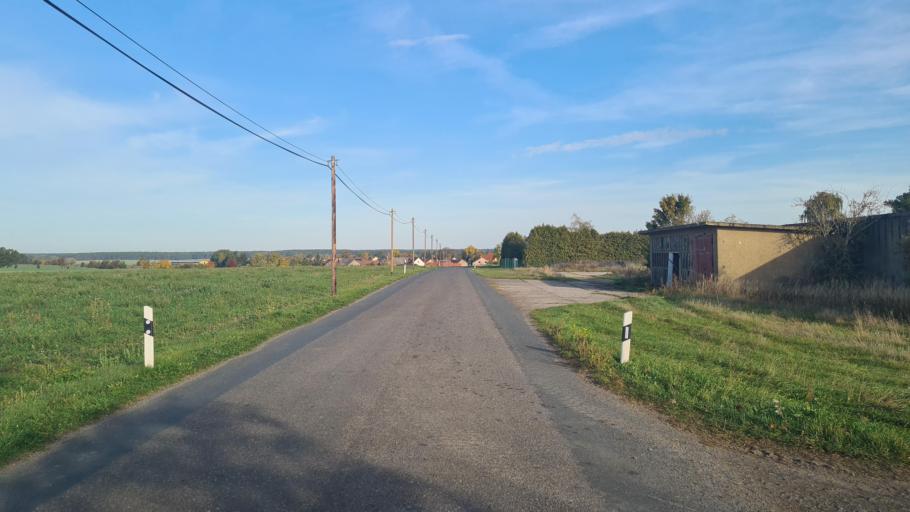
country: DE
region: Brandenburg
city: Dahme
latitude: 51.8779
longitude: 13.3826
